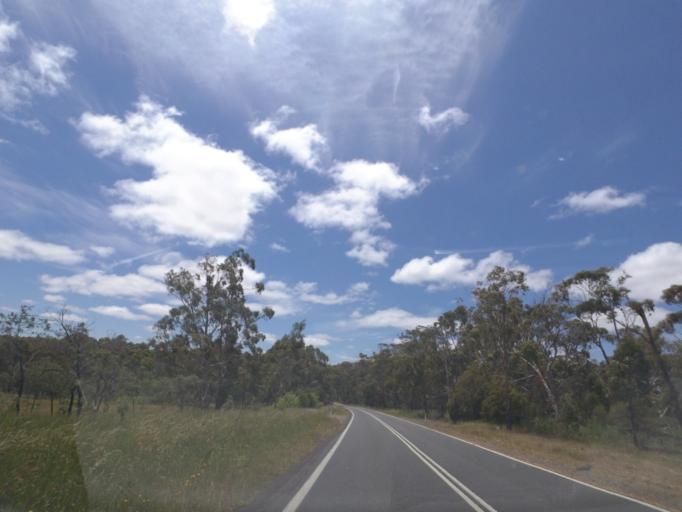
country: AU
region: Victoria
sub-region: Mount Alexander
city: Castlemaine
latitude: -37.3163
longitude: 144.1656
